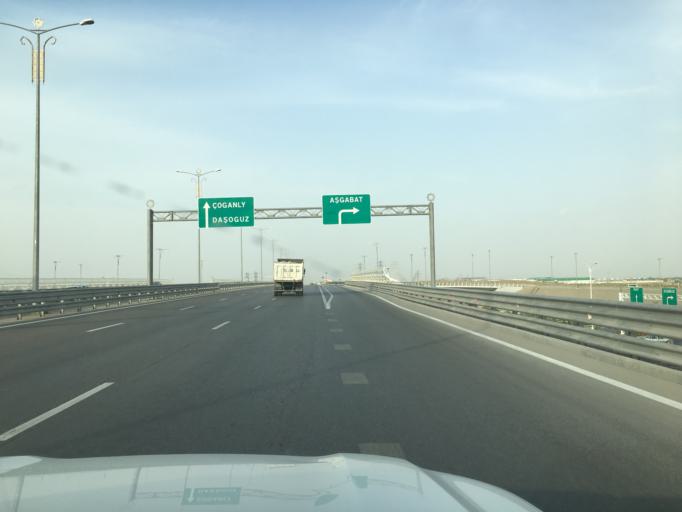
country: TM
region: Ahal
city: Annau
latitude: 37.9118
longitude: 58.4846
